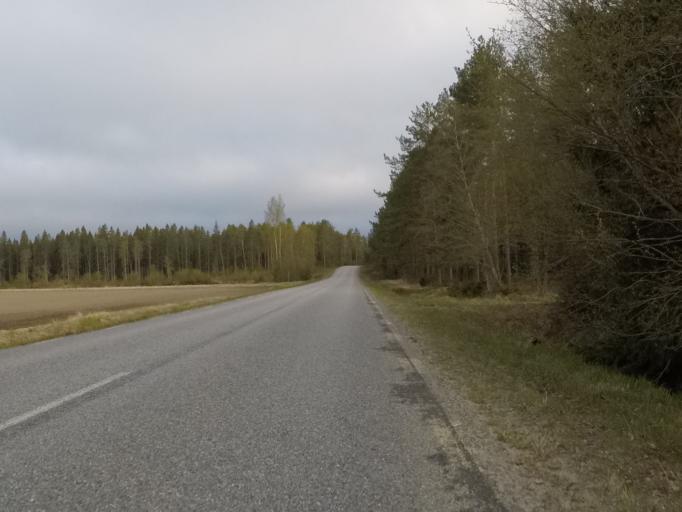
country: SE
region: Vaesterbotten
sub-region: Umea Kommun
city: Saevar
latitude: 63.9416
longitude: 20.7878
